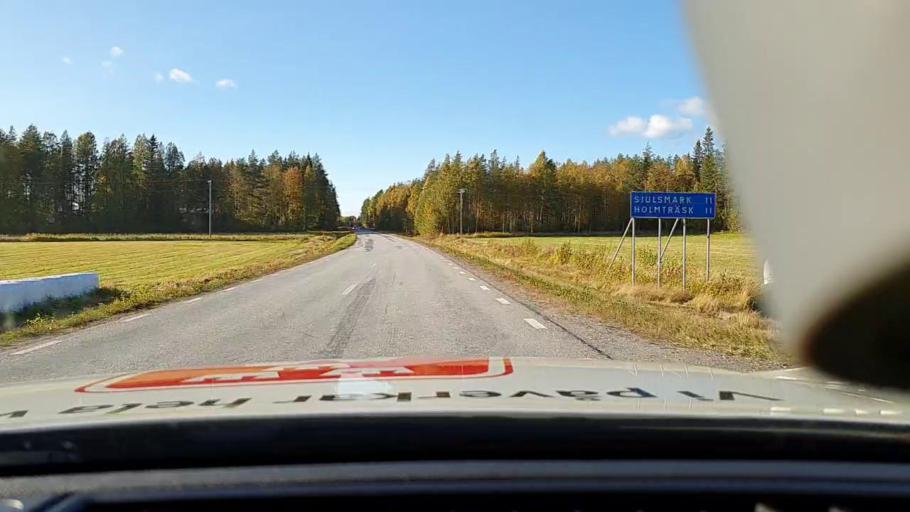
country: SE
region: Norrbotten
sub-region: Pitea Kommun
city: Norrfjarden
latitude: 65.4342
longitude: 21.4835
